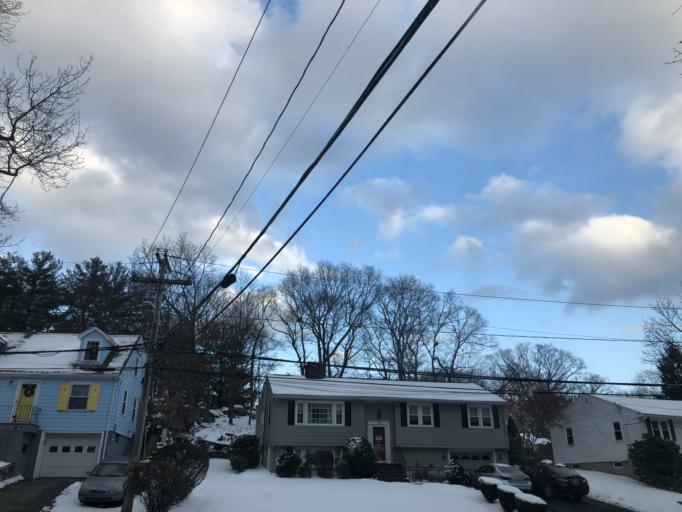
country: US
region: Massachusetts
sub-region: Middlesex County
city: Arlington
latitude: 42.4283
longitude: -71.1618
